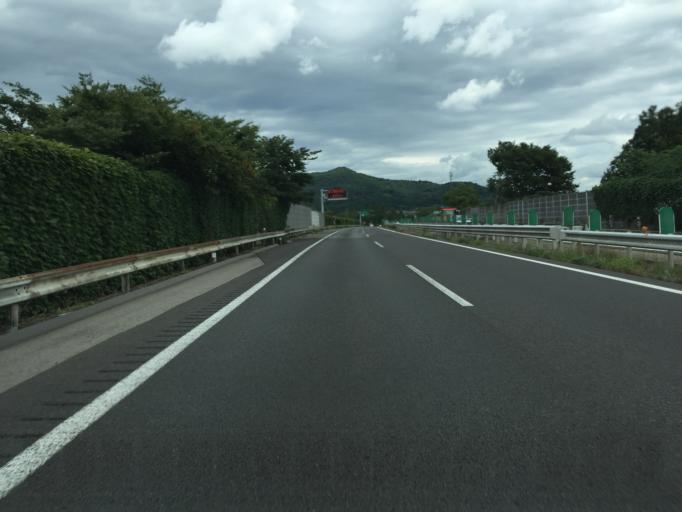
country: JP
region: Miyagi
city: Shiroishi
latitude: 38.0339
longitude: 140.6276
